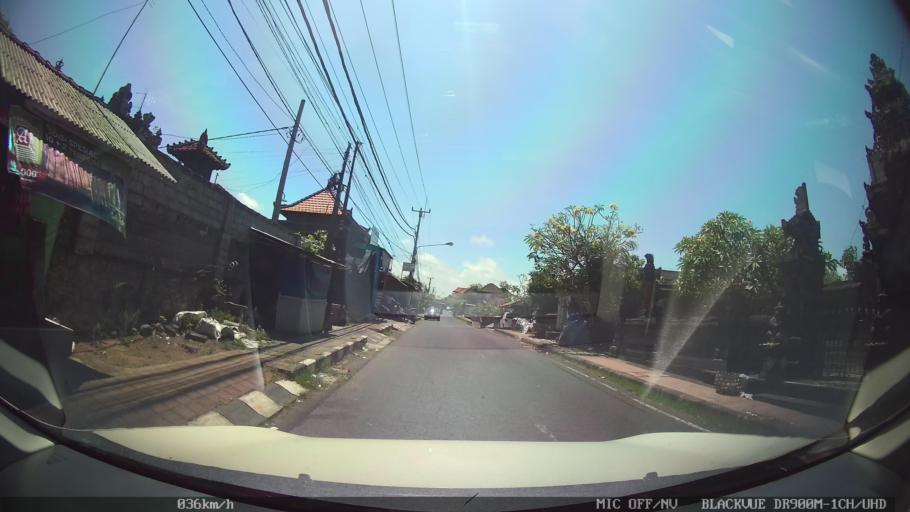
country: ID
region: Bali
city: Klungkung
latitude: -8.5761
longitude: 115.3504
